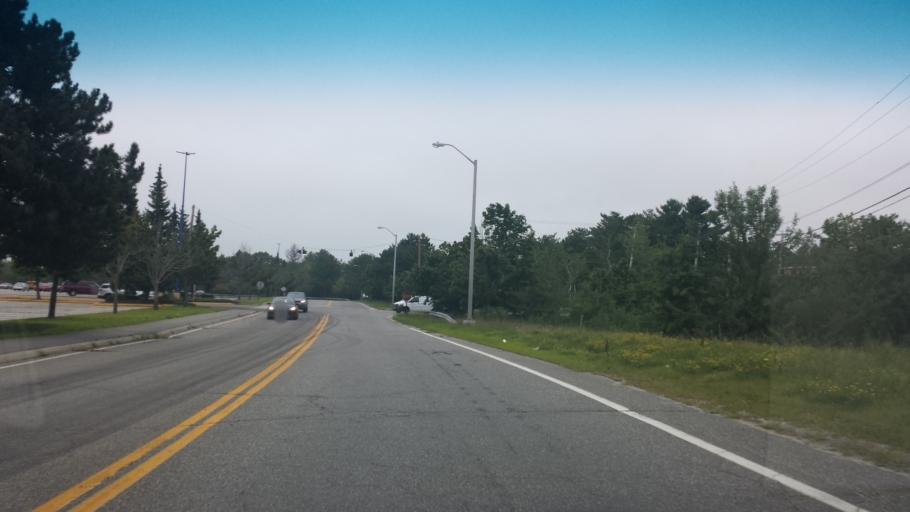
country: US
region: Maine
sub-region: Cumberland County
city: South Portland Gardens
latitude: 43.6301
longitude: -70.3317
